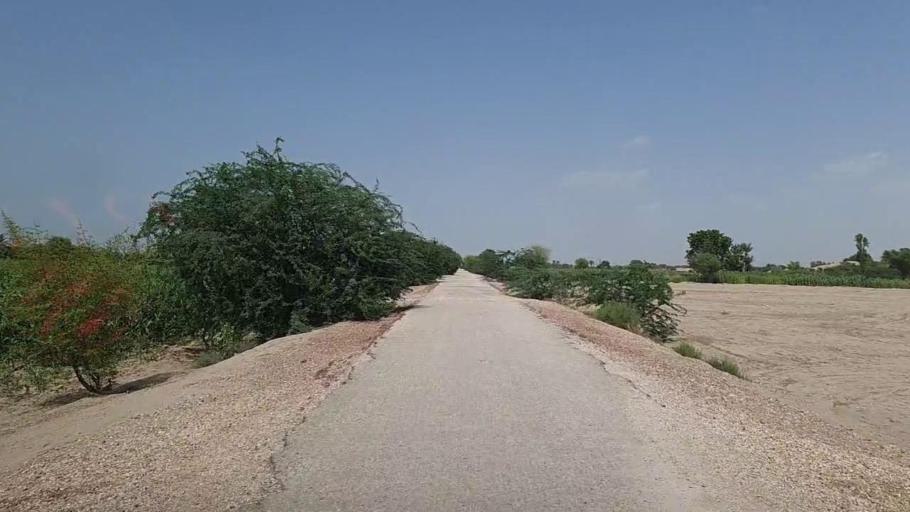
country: PK
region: Sindh
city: Pad Idan
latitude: 26.7895
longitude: 68.3512
